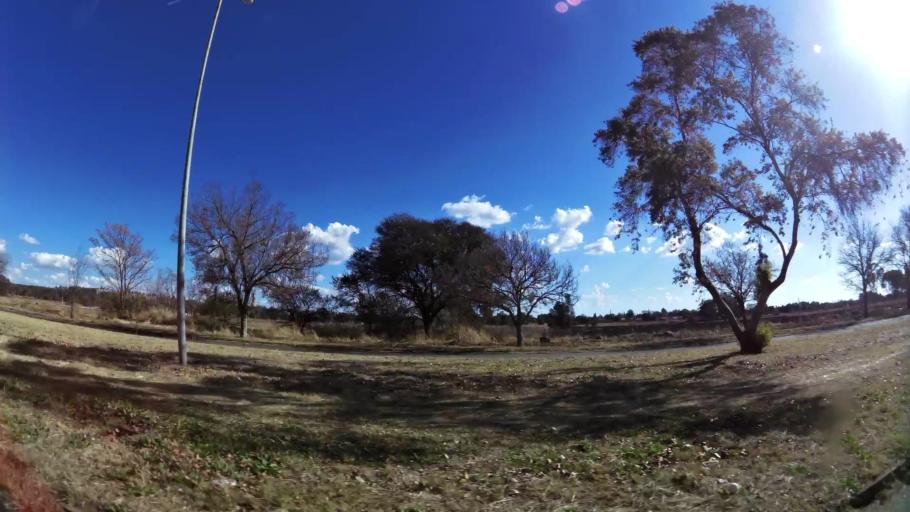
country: ZA
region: Gauteng
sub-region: West Rand District Municipality
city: Carletonville
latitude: -26.3709
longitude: 27.3961
